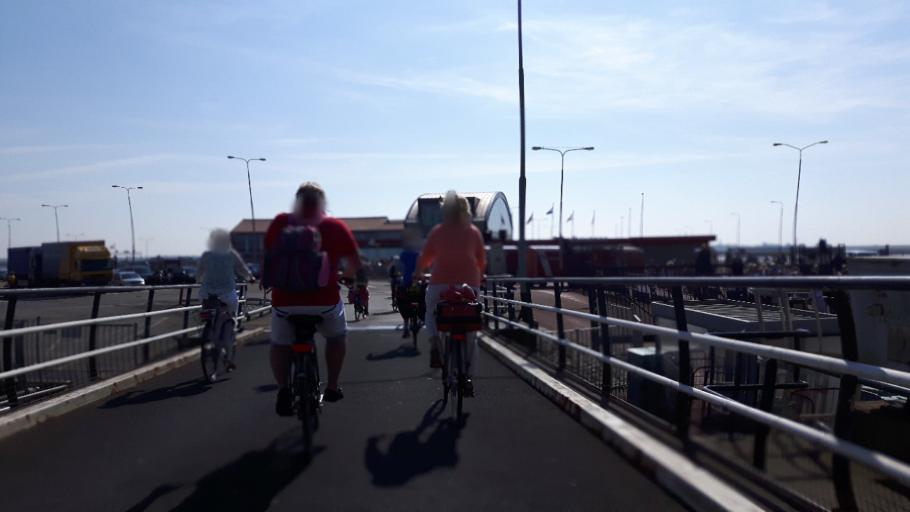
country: NL
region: Friesland
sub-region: Gemeente Dongeradeel
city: Holwerd
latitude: 53.3953
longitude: 5.8792
